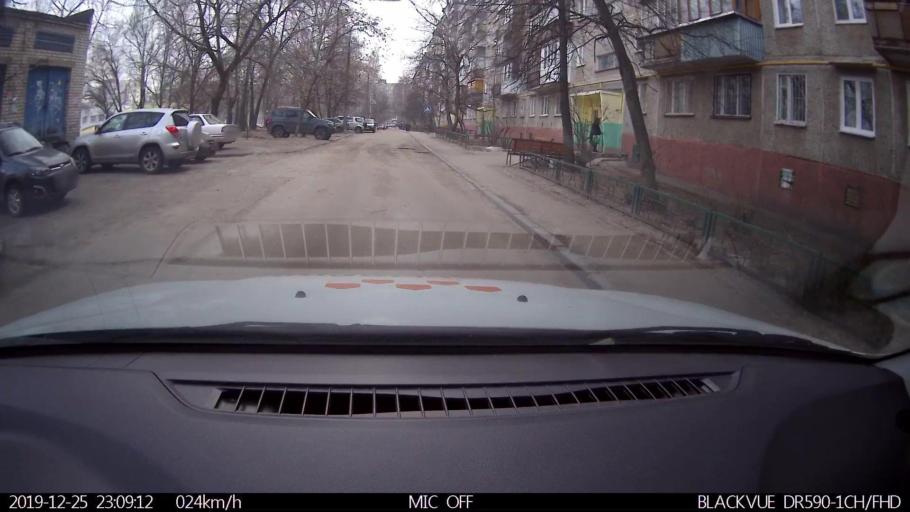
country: RU
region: Nizjnij Novgorod
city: Gorbatovka
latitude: 56.3626
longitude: 43.8196
